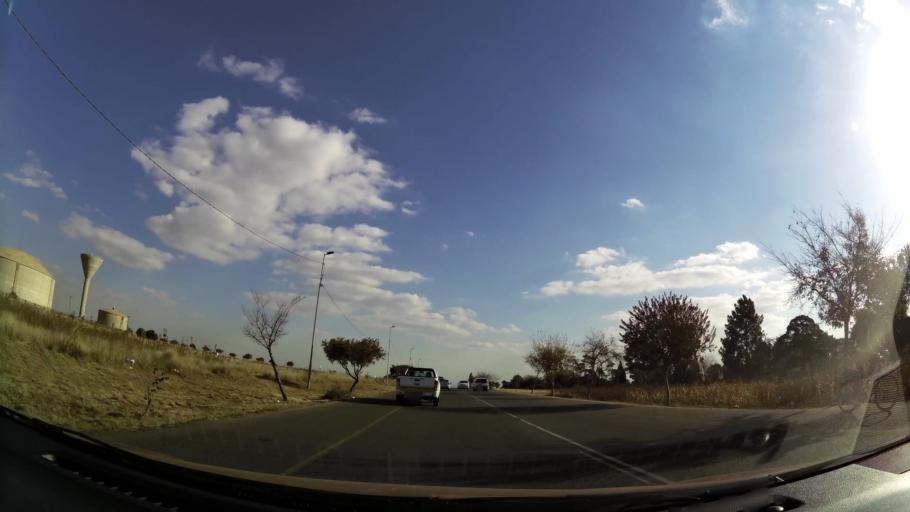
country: ZA
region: Gauteng
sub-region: City of Johannesburg Metropolitan Municipality
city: Midrand
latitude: -26.0120
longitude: 28.1646
